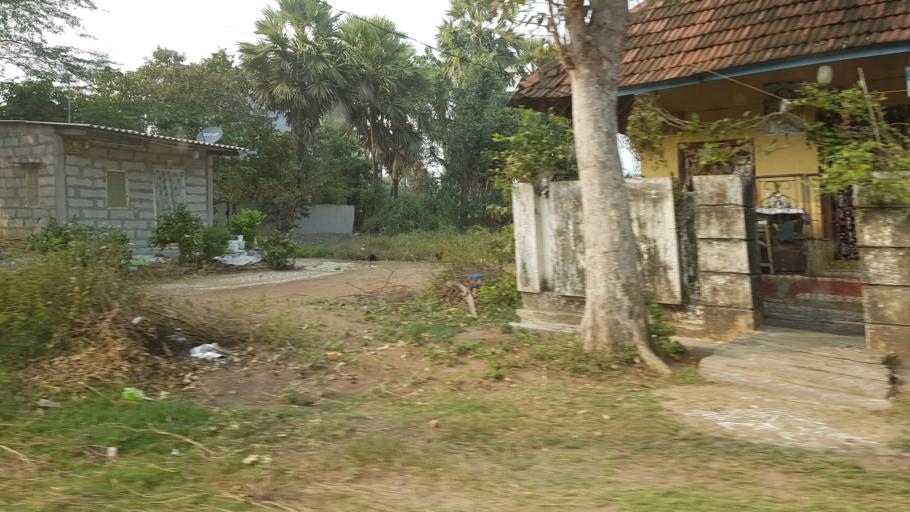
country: IN
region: Andhra Pradesh
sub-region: West Godavari
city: Akividu
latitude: 16.5298
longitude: 81.3889
